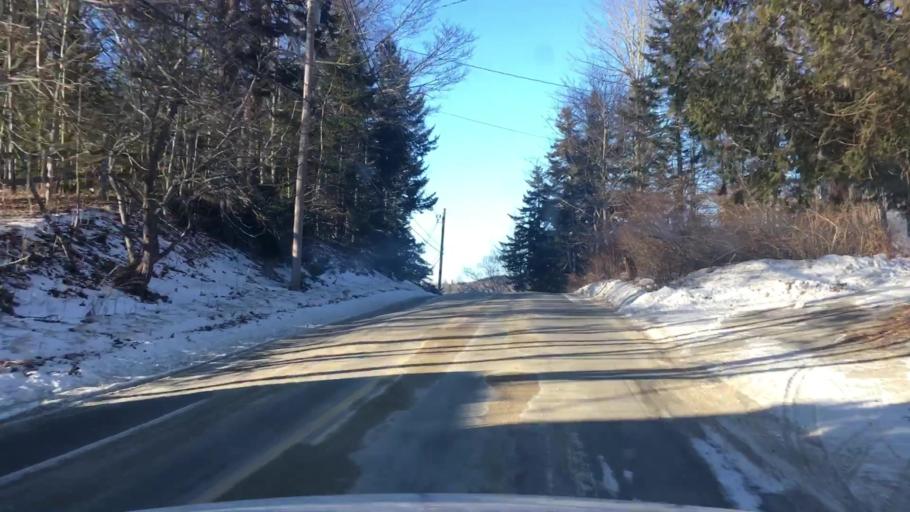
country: US
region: Maine
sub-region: Hancock County
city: Castine
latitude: 44.3453
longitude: -68.7458
